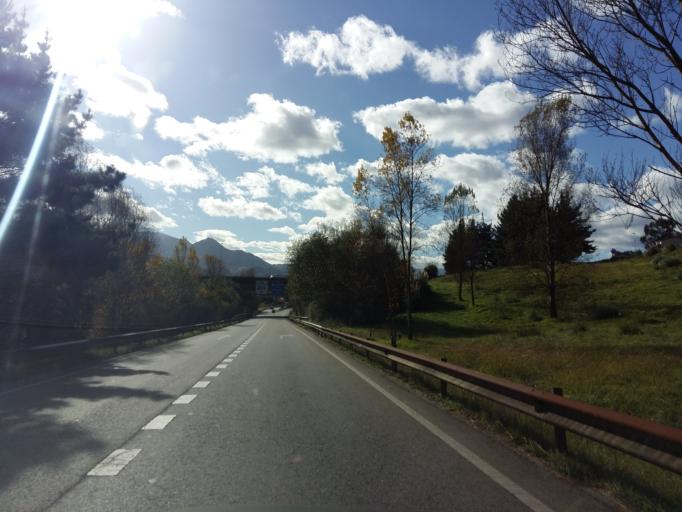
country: ES
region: Asturias
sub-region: Province of Asturias
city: Oviedo
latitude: 43.3465
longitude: -5.8622
